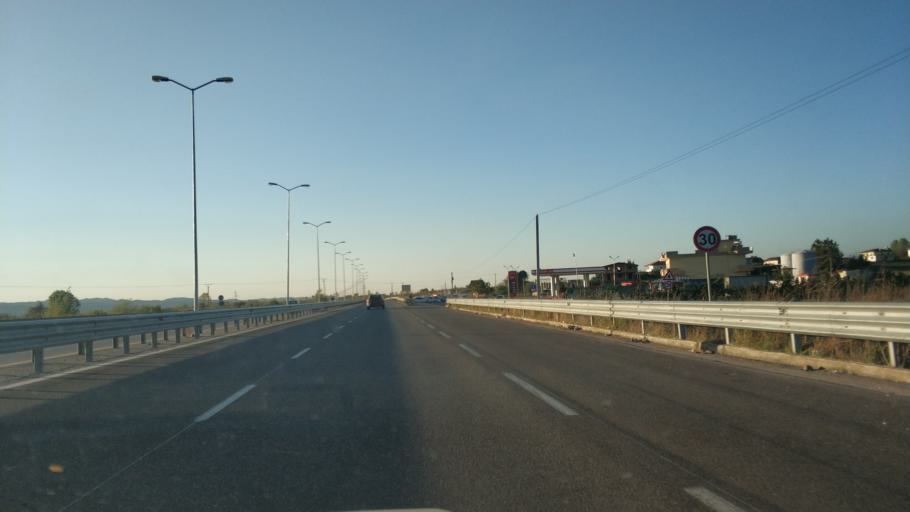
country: AL
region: Tirane
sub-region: Rrethi i Kavajes
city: Gose e Madhe
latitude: 41.0826
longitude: 19.6205
